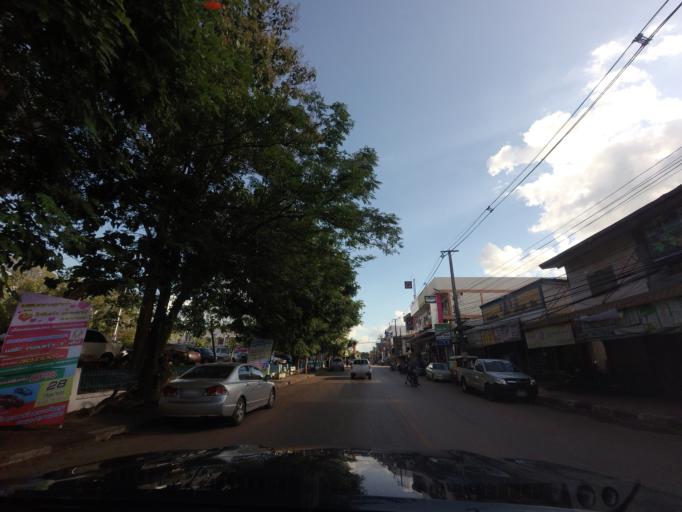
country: TH
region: Changwat Udon Thani
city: Ban Dung
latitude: 17.7012
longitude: 103.2578
